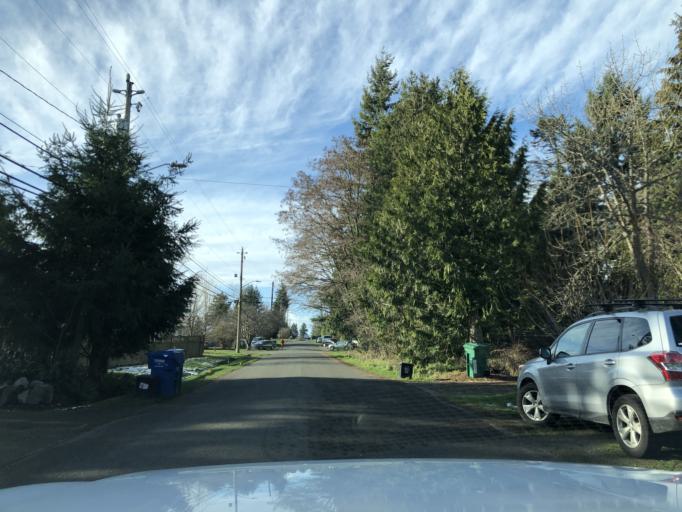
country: US
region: Washington
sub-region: King County
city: Lake Forest Park
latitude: 47.7157
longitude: -122.3048
